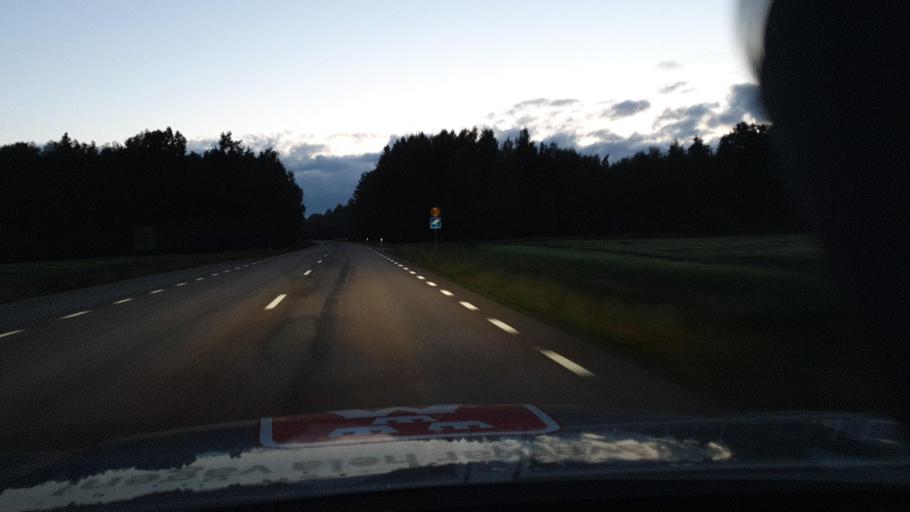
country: SE
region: OErebro
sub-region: Karlskoga Kommun
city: Karlskoga
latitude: 59.3805
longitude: 14.4929
